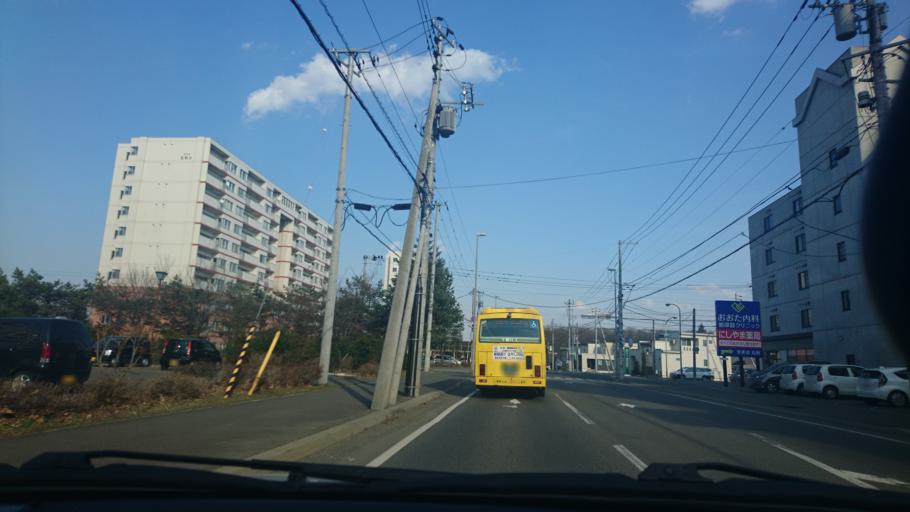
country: JP
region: Hokkaido
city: Obihiro
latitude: 42.9249
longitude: 143.1702
